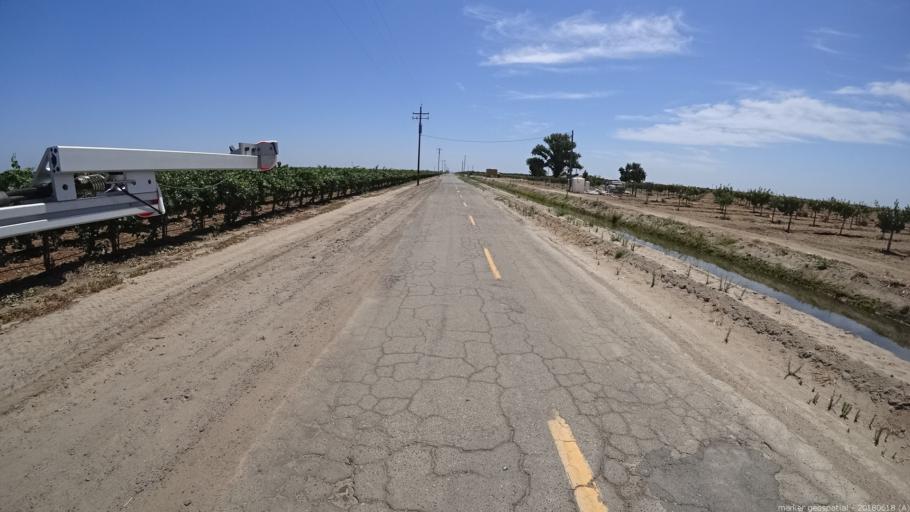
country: US
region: California
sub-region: Madera County
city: Madera
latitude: 36.8949
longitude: -120.1601
